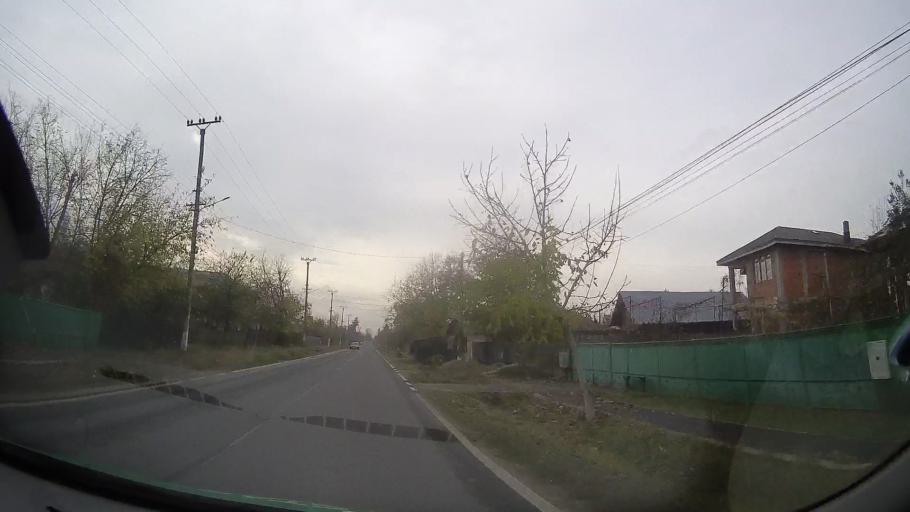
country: RO
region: Ilfov
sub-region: Comuna Gruiu
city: Silistea Snagovului
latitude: 44.7497
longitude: 26.1902
